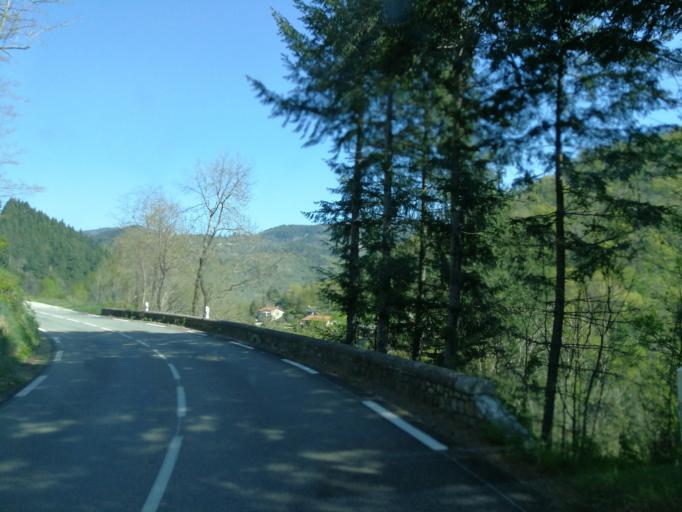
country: FR
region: Rhone-Alpes
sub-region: Departement de l'Ardeche
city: Le Cheylard
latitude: 44.8976
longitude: 4.4852
